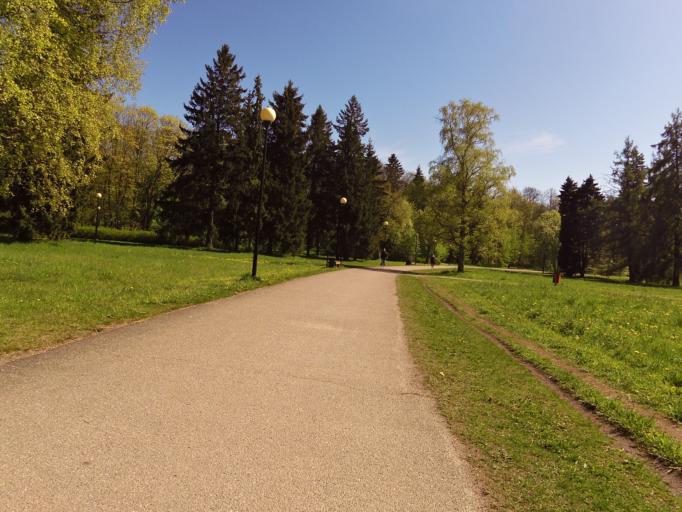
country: EE
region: Harju
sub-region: Tallinna linn
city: Tallinn
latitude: 59.4405
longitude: 24.8012
